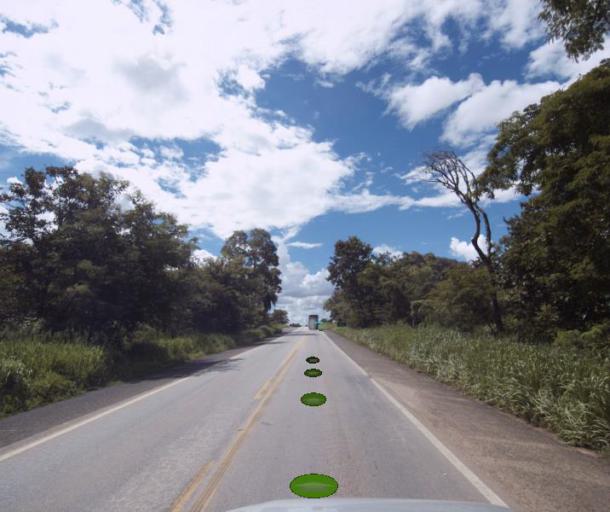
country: BR
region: Goias
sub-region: Porangatu
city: Porangatu
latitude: -13.8693
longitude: -49.0521
